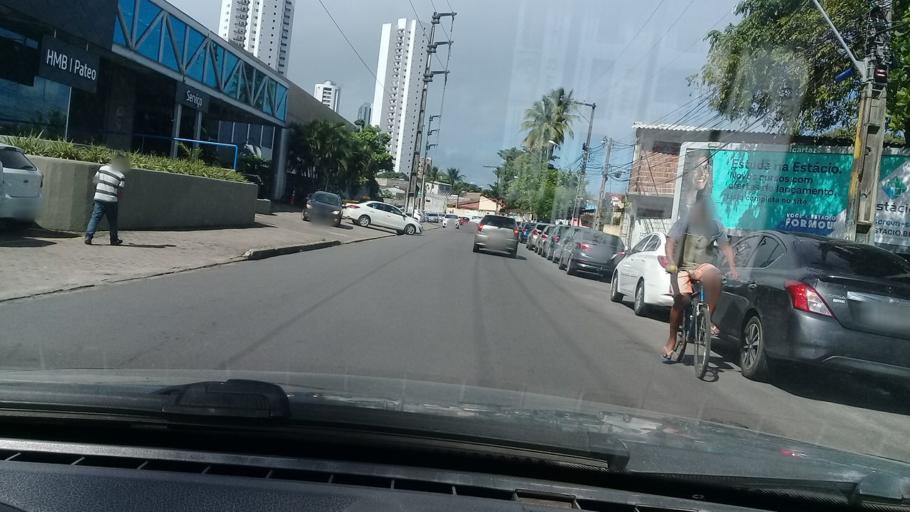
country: BR
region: Pernambuco
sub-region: Recife
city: Recife
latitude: -8.0652
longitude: -34.9077
